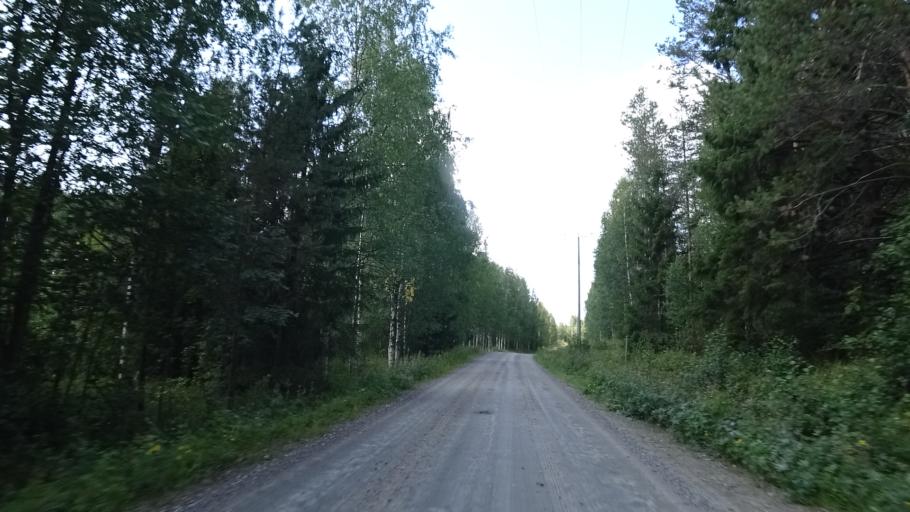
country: FI
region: North Karelia
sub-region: Joensuu
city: Ilomantsi
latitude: 62.9301
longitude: 31.3149
